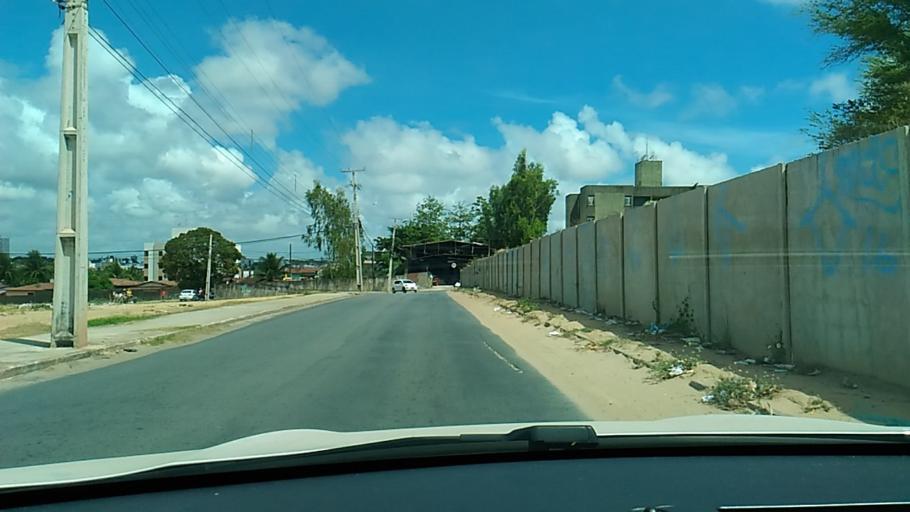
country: BR
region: Paraiba
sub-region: Joao Pessoa
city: Joao Pessoa
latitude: -7.1609
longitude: -34.8422
